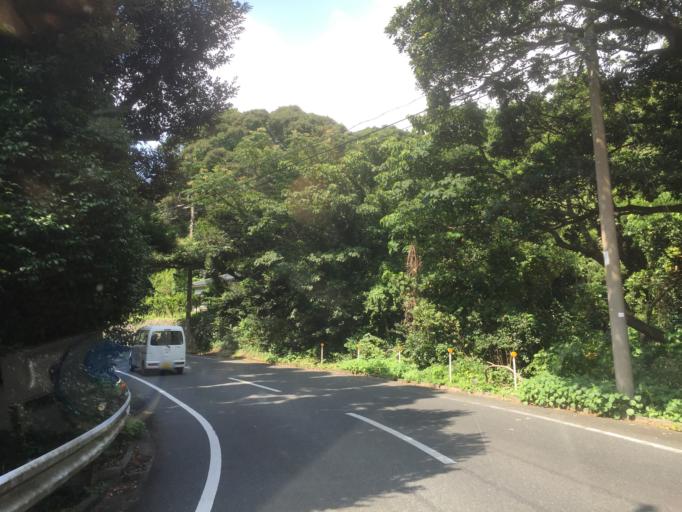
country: JP
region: Shizuoka
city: Shimoda
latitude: 34.0551
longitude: 139.5331
